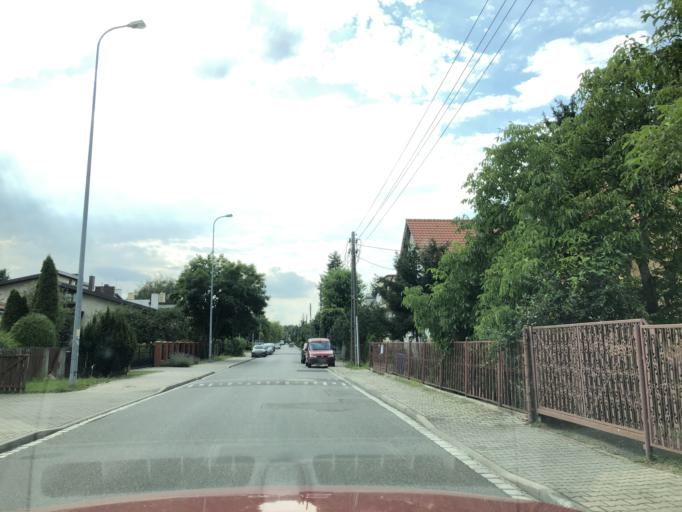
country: PL
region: Lower Silesian Voivodeship
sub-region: Powiat wroclawski
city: Smolec
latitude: 51.1570
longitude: 16.9021
